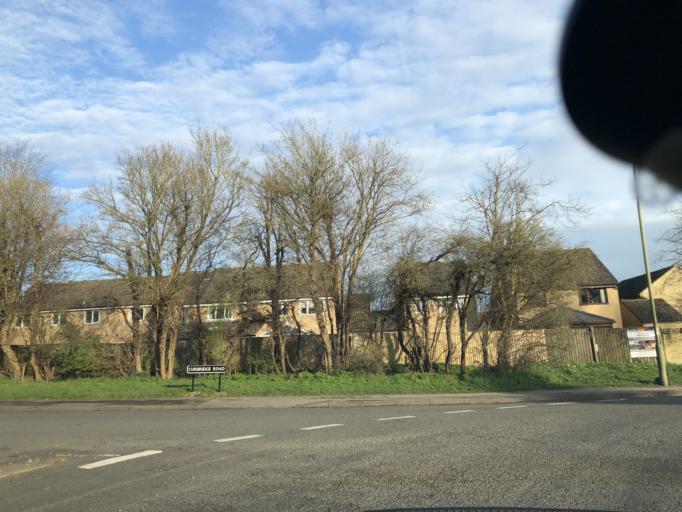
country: GB
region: England
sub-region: Oxfordshire
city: Witney
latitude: 51.7799
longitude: -1.5104
